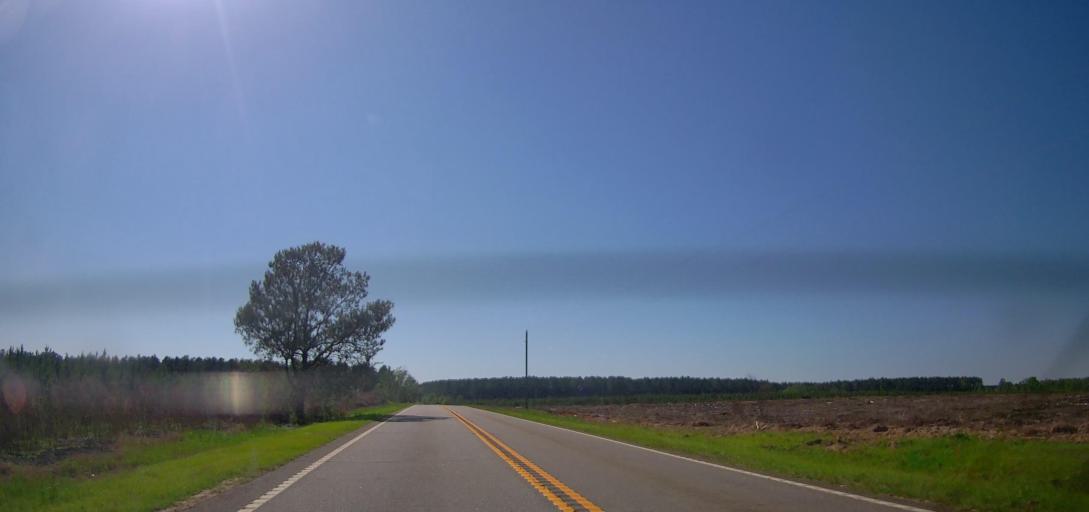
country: US
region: Georgia
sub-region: Dooly County
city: Unadilla
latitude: 32.2542
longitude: -83.6307
